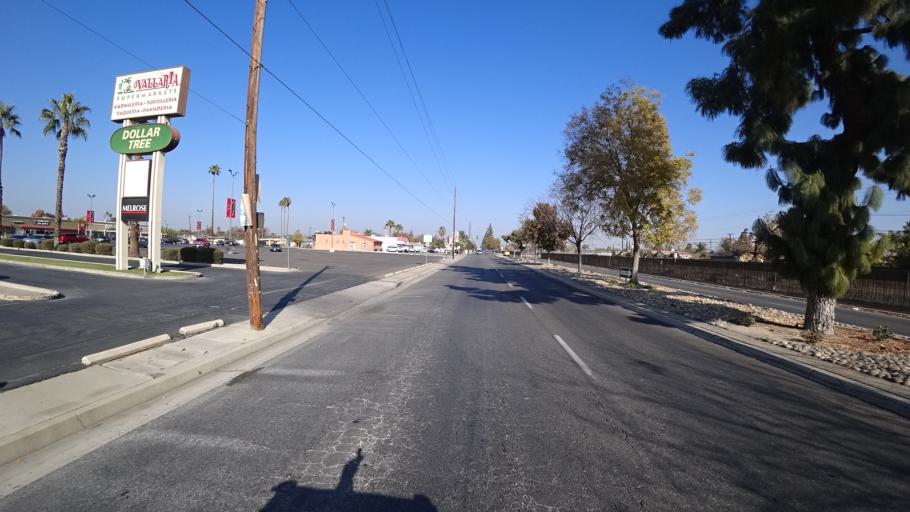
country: US
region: California
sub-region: Kern County
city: Bakersfield
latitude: 35.3310
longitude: -119.0213
